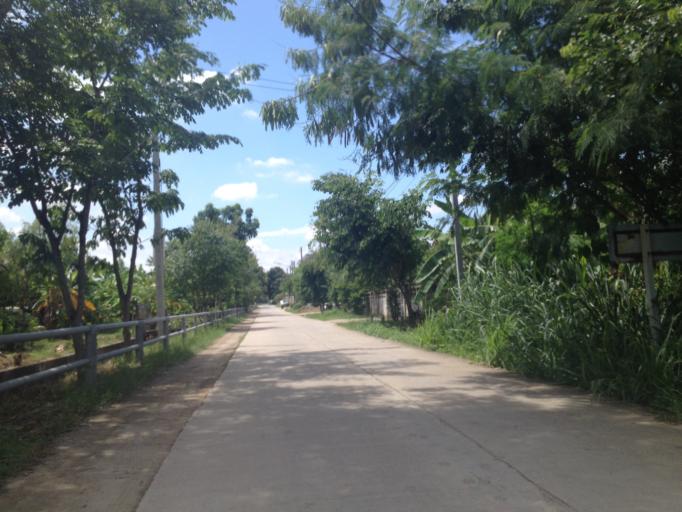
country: TH
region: Chiang Mai
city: Chiang Mai
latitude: 18.7613
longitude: 98.9487
